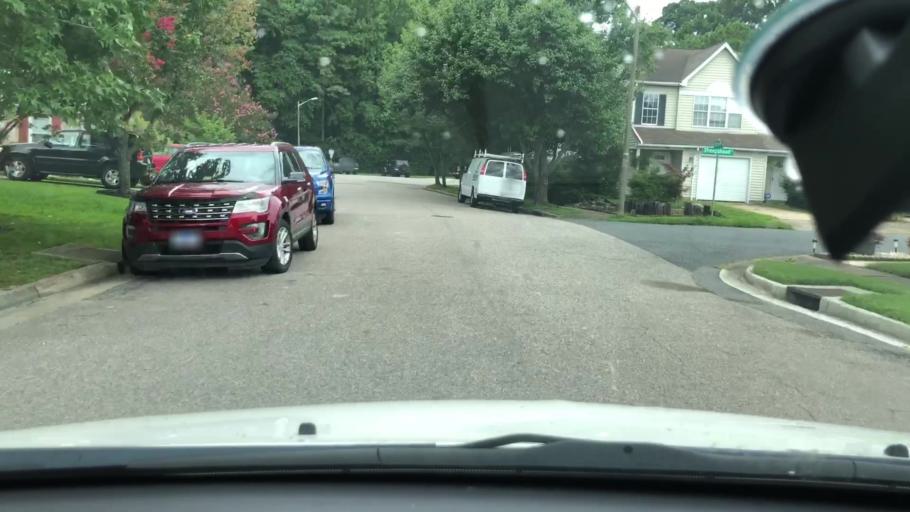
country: US
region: Virginia
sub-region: City of Virginia Beach
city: Virginia Beach
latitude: 36.8463
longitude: -76.1173
